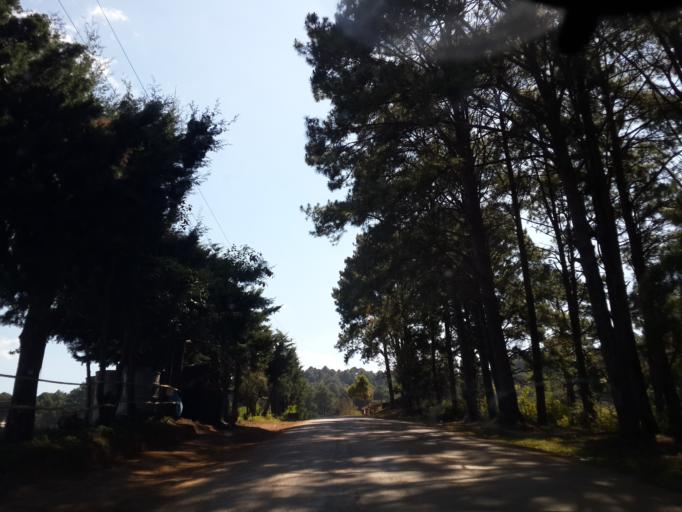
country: TH
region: Chiang Mai
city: Fang
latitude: 19.9334
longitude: 99.0426
